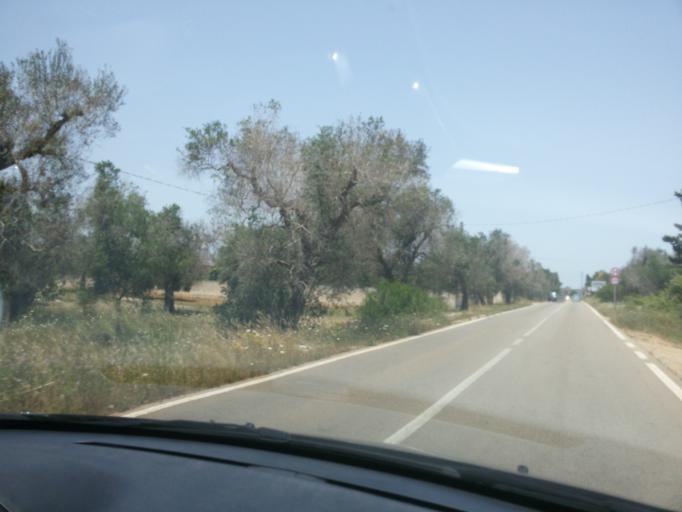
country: IT
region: Apulia
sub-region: Provincia di Lecce
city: Veglie
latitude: 40.3237
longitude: 17.9248
